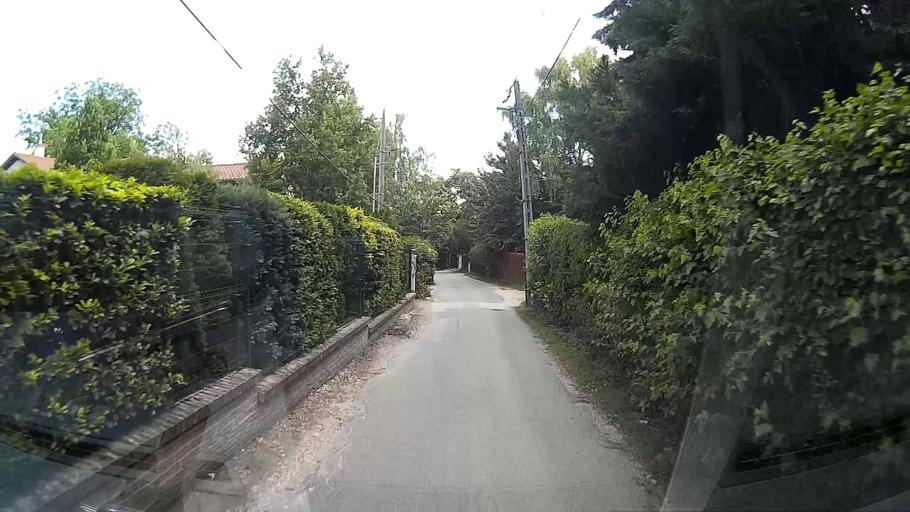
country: HU
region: Pest
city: Szentendre
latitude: 47.6739
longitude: 19.0609
